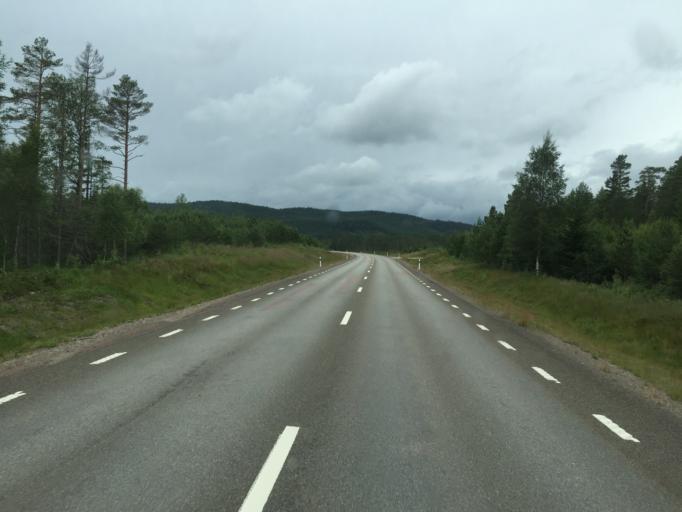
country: SE
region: Dalarna
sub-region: Malung-Saelens kommun
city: Malung
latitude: 60.6485
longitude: 13.6436
